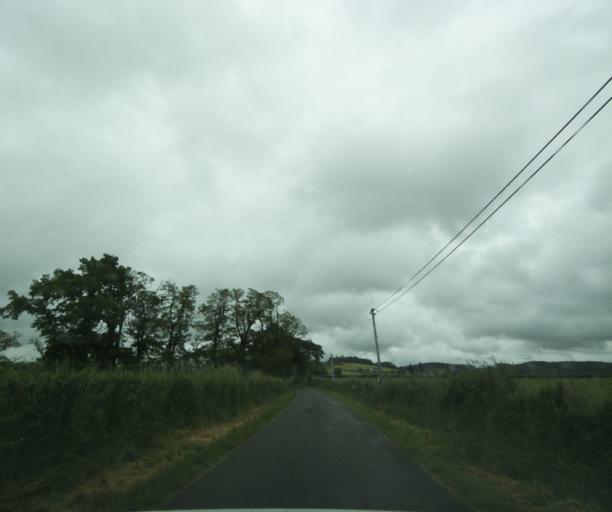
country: FR
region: Bourgogne
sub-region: Departement de Saone-et-Loire
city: Matour
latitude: 46.4598
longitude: 4.4447
